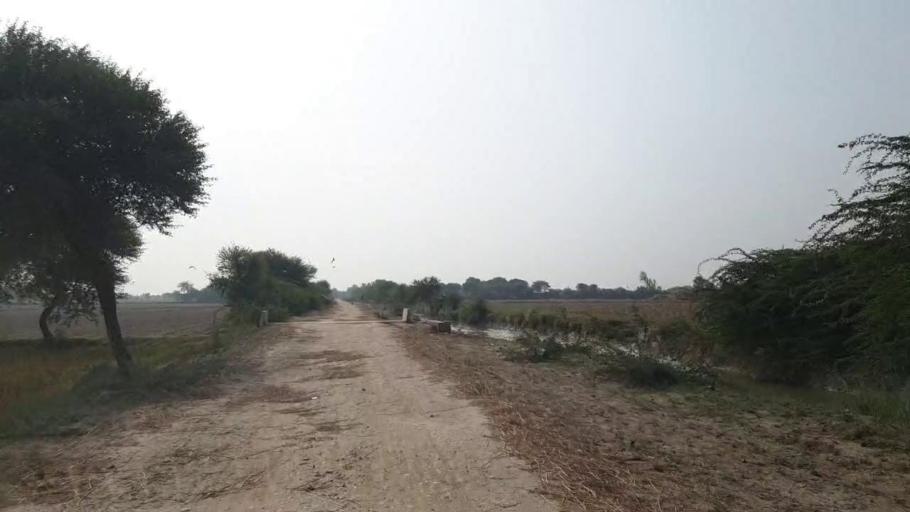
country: PK
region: Sindh
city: Kario
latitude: 24.7606
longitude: 68.5637
